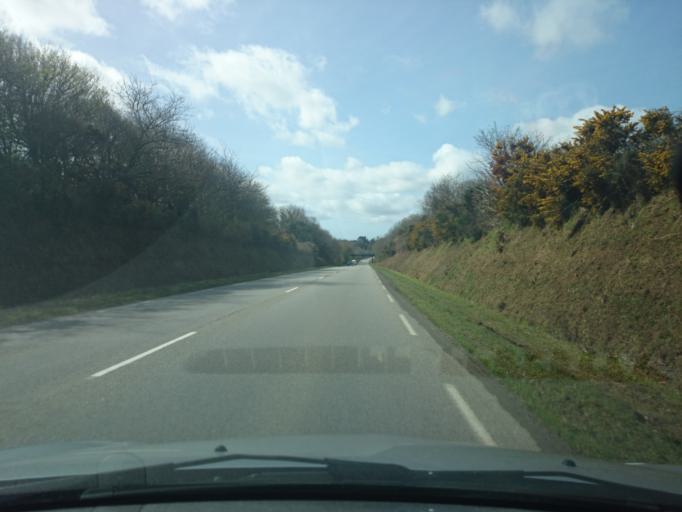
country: FR
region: Brittany
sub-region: Departement du Finistere
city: Gouesnou
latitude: 48.4522
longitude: -4.4490
